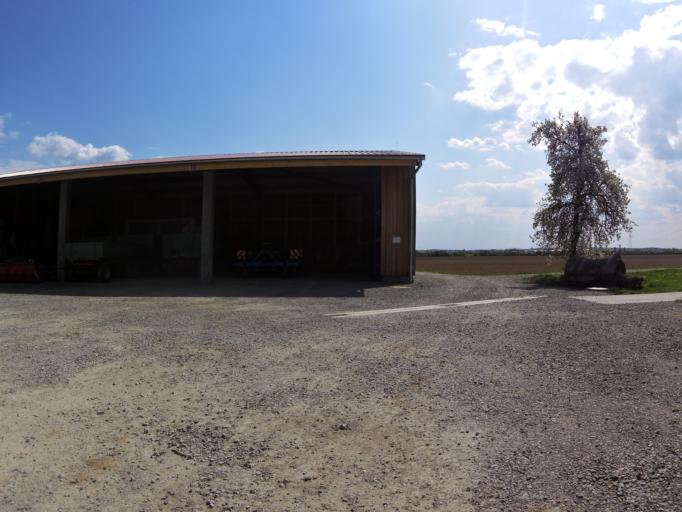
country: DE
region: Bavaria
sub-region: Regierungsbezirk Unterfranken
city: Oberpleichfeld
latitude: 49.8529
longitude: 10.1008
